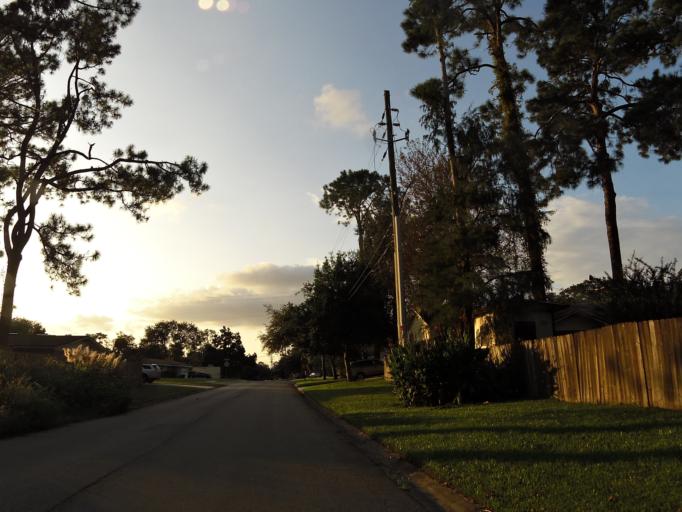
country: US
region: Florida
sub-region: Clay County
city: Orange Park
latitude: 30.2039
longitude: -81.6232
